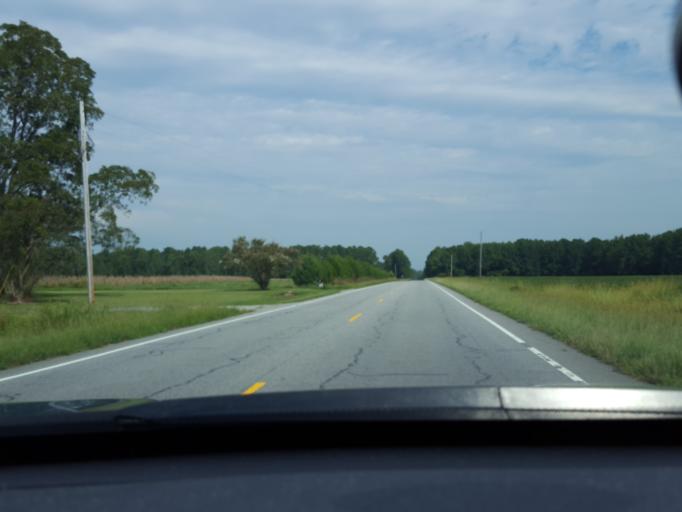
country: US
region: North Carolina
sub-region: Washington County
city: Plymouth
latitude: 35.9447
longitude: -76.7447
